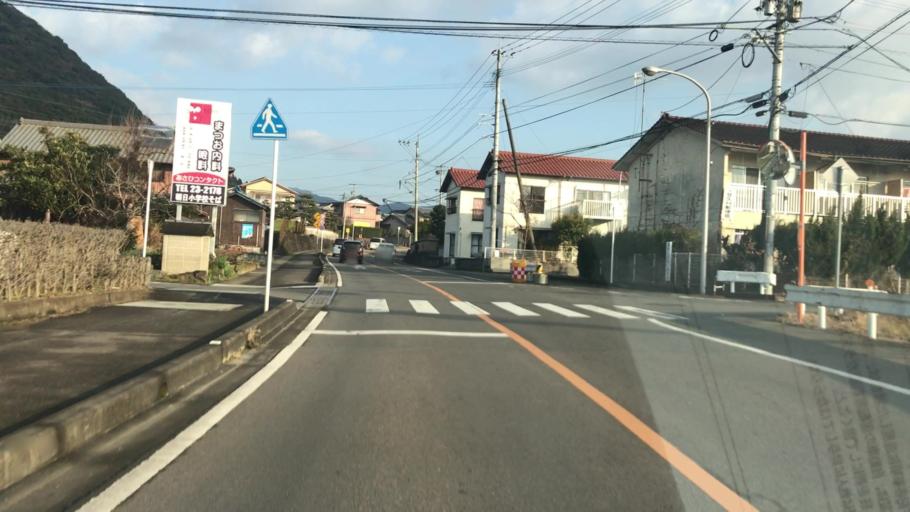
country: JP
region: Saga Prefecture
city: Takeocho-takeo
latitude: 33.2045
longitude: 130.0248
